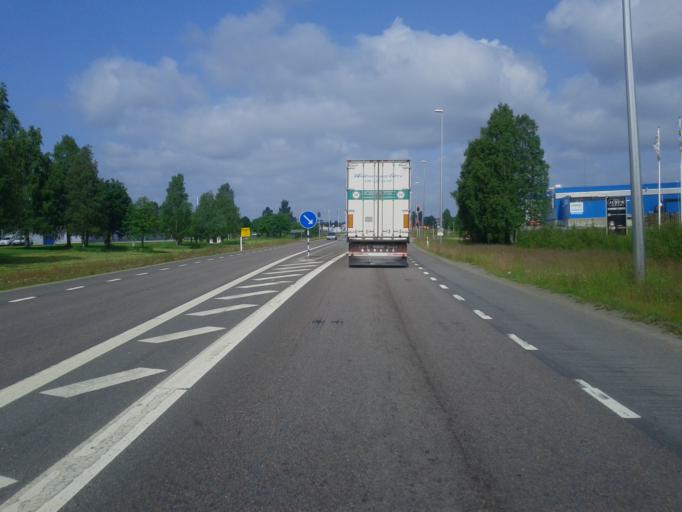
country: SE
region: Vaesterbotten
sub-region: Skelleftea Kommun
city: Skelleftea
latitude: 64.7346
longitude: 20.9689
